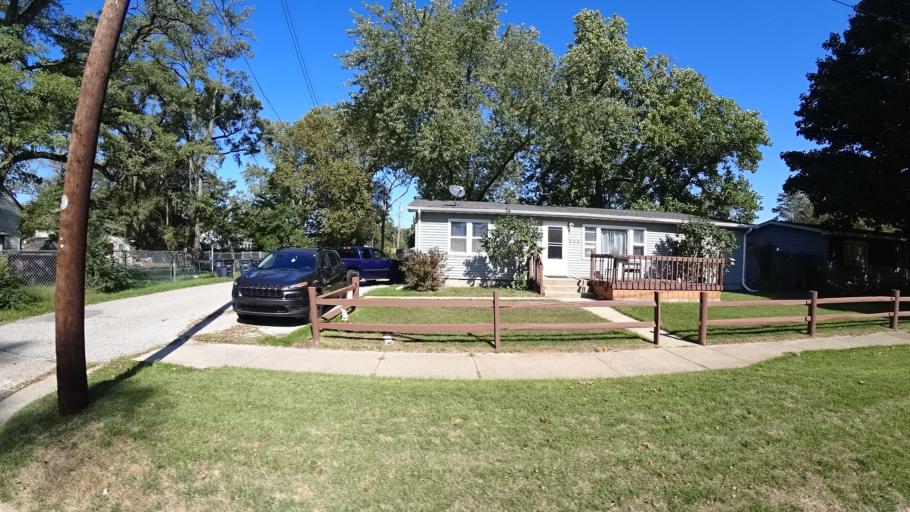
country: US
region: Indiana
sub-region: LaPorte County
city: Michigan City
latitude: 41.7060
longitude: -86.8836
